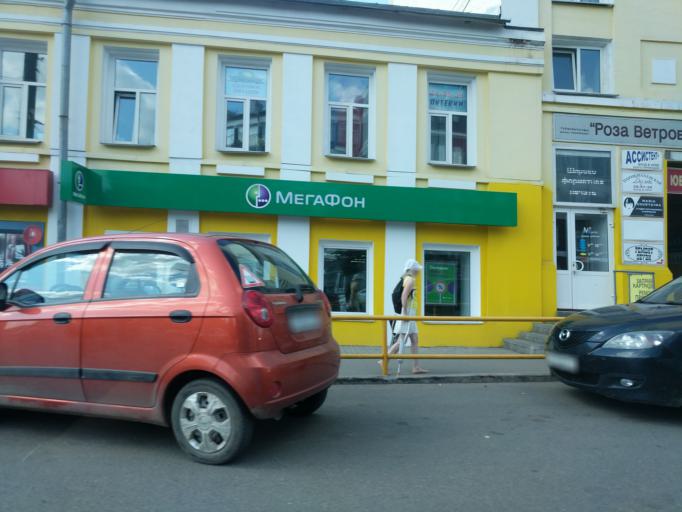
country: RU
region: Kirov
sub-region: Kirovo-Chepetskiy Rayon
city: Kirov
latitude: 58.6042
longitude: 49.6808
